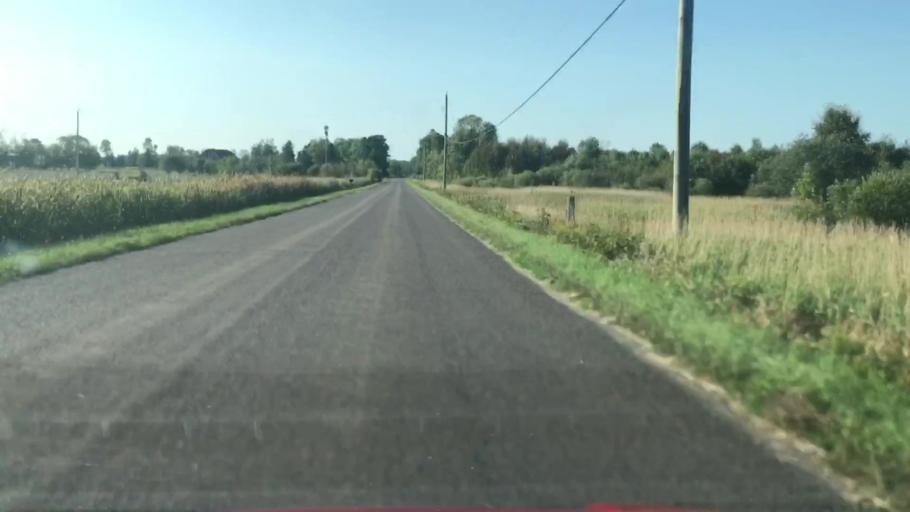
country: US
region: Michigan
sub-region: Chippewa County
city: Sault Ste. Marie
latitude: 46.2867
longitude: -84.0578
